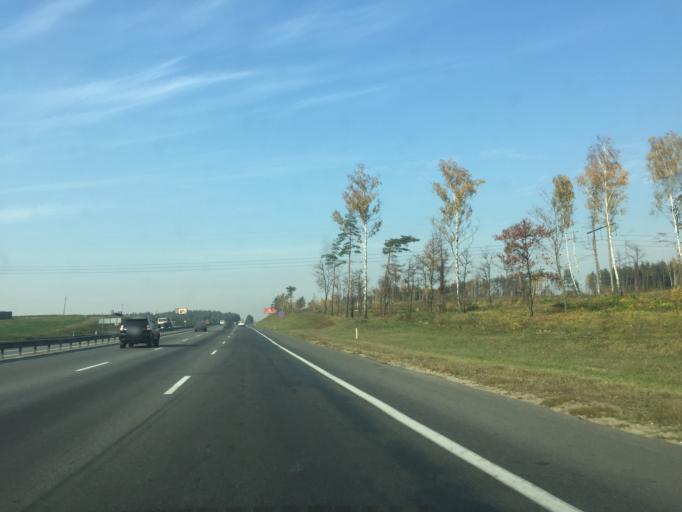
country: BY
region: Minsk
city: Pryvol'ny
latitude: 53.8113
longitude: 27.7803
